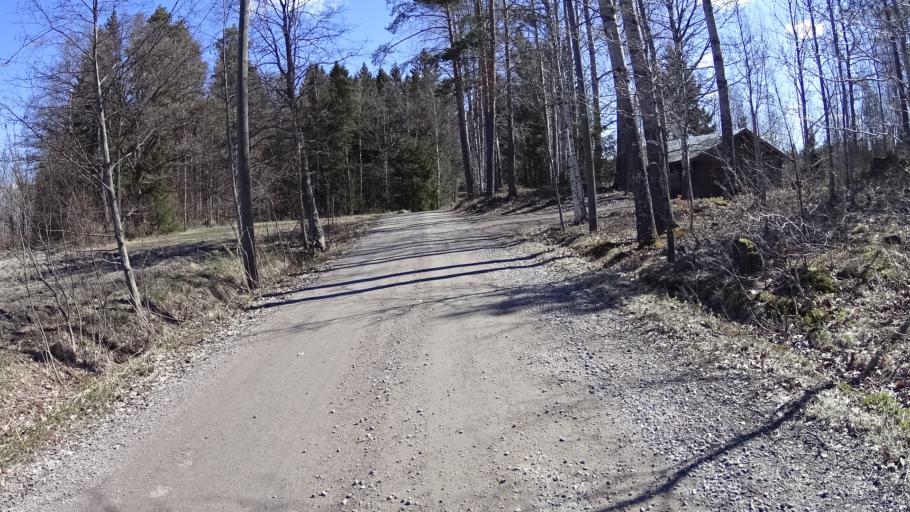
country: FI
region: Uusimaa
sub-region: Helsinki
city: Espoo
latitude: 60.2394
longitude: 24.6850
